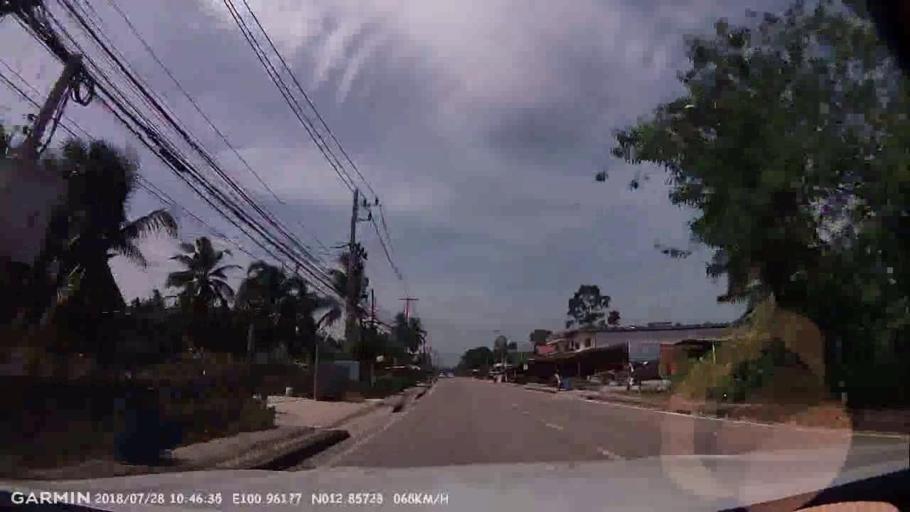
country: TH
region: Chon Buri
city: Phatthaya
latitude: 12.8574
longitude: 100.9616
